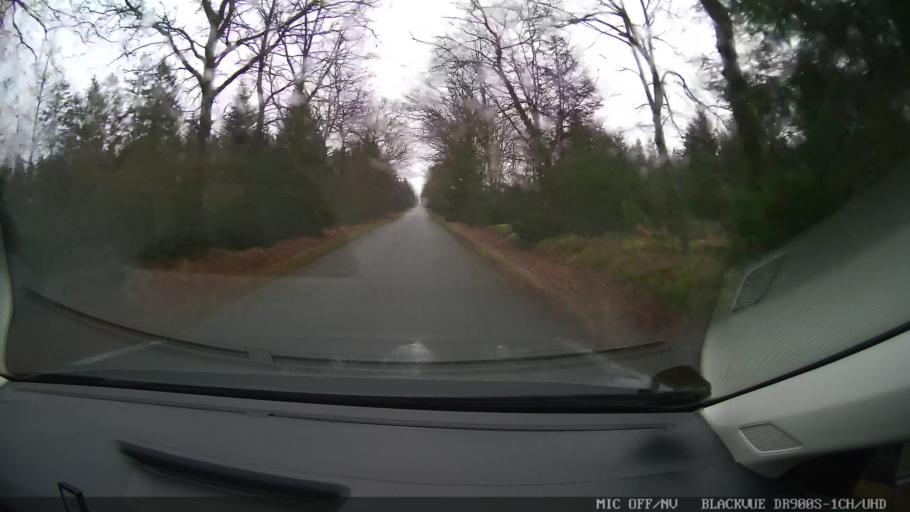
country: DK
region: Central Jutland
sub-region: Viborg Kommune
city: Karup
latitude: 56.2351
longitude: 9.1215
